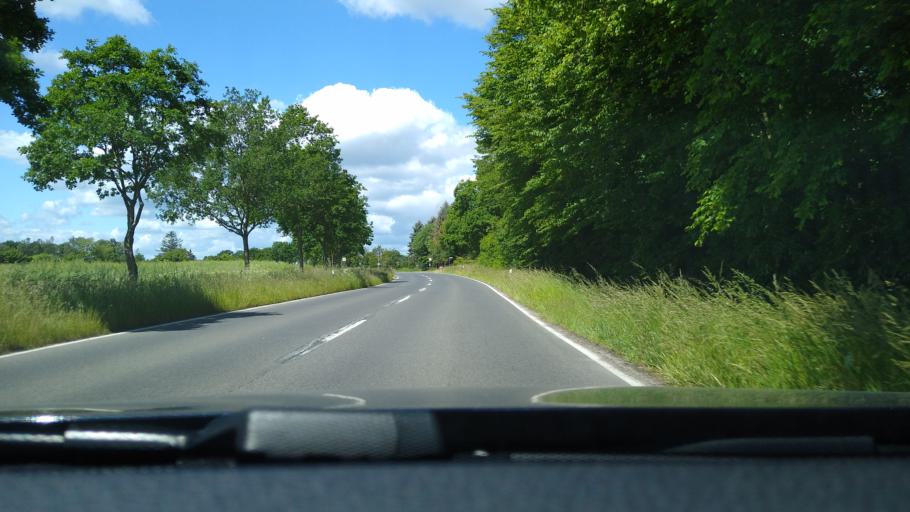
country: DE
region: Schleswig-Holstein
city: Kellenhusen
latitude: 54.2135
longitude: 11.0578
